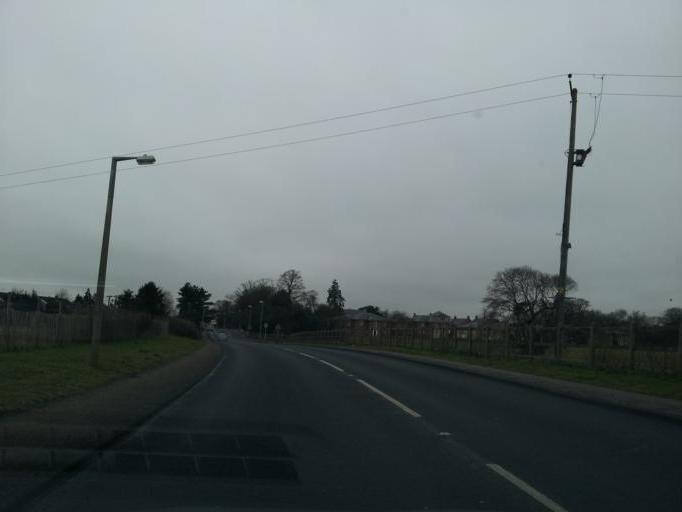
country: GB
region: England
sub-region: Essex
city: Manningtree
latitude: 51.9424
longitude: 1.0462
